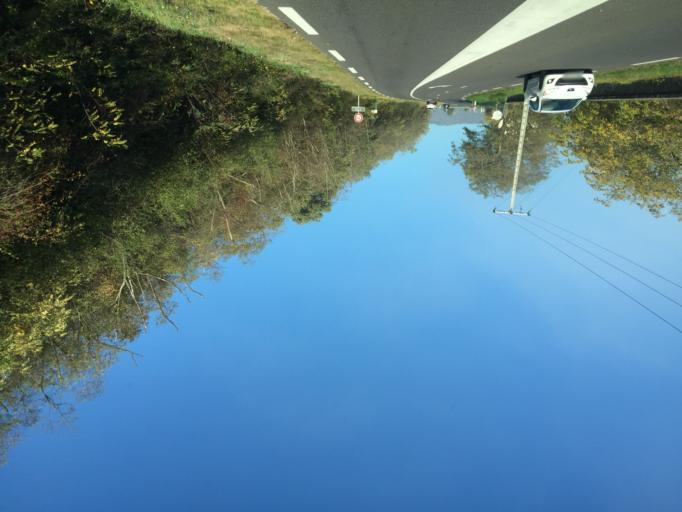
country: FR
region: Rhone-Alpes
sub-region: Departement de la Loire
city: Chateauneuf
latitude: 45.5466
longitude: 4.6405
